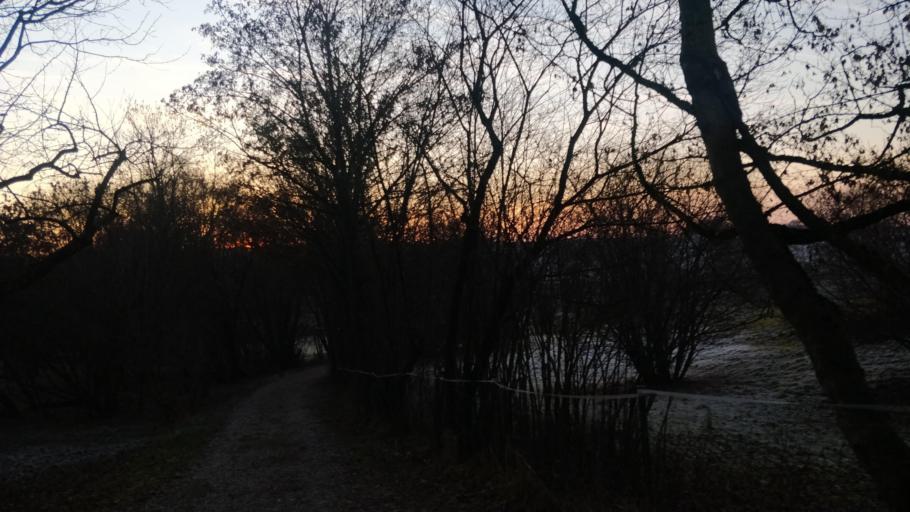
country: DE
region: Bavaria
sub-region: Upper Bavaria
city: Obertaufkirchen
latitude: 48.2619
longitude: 12.2741
